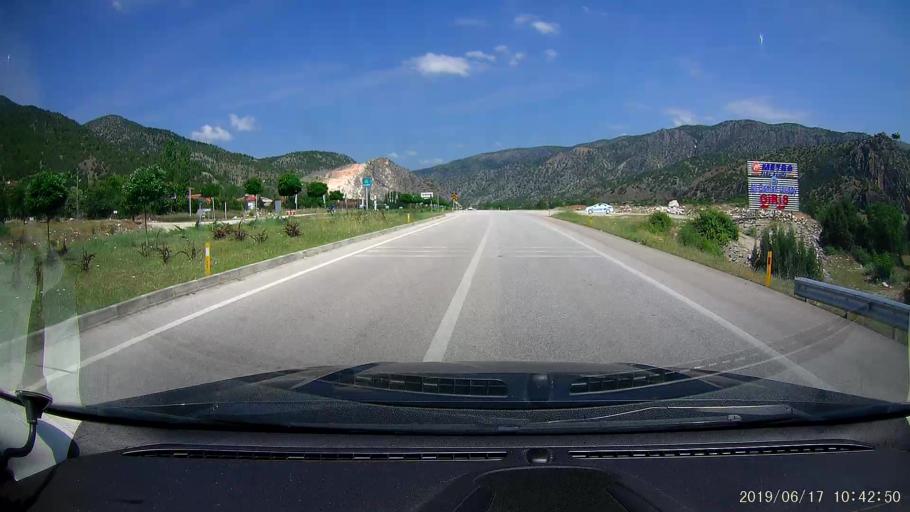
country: TR
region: Corum
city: Hacihamza
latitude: 41.0534
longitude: 34.5461
